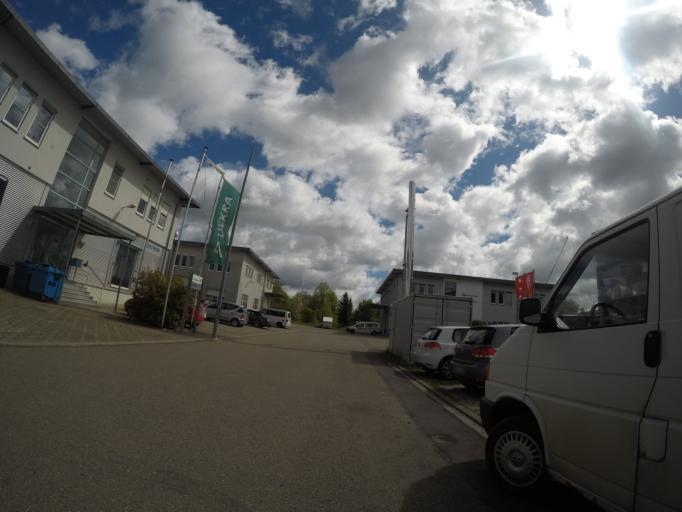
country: DE
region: Baden-Wuerttemberg
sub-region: Tuebingen Region
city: Dornstadt
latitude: 48.4527
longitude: 9.9699
